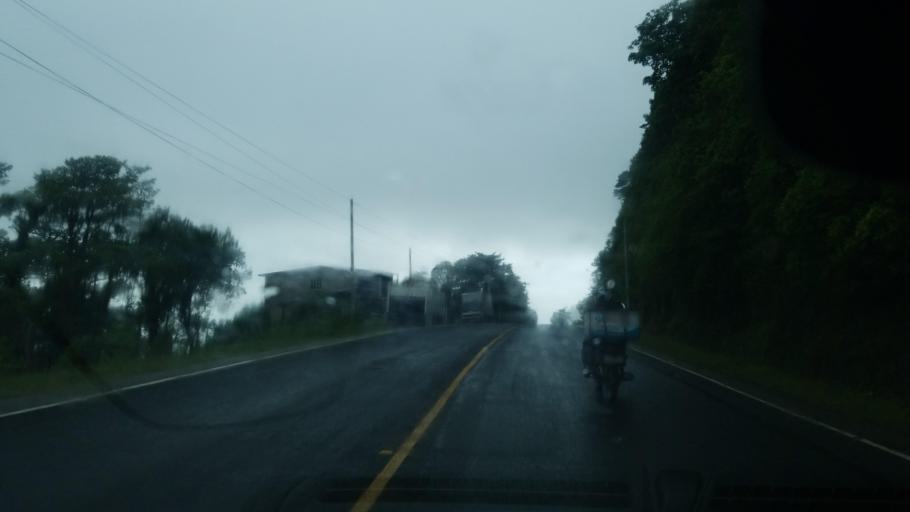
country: HN
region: Ocotepeque
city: La Labor
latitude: 14.4659
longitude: -89.0766
